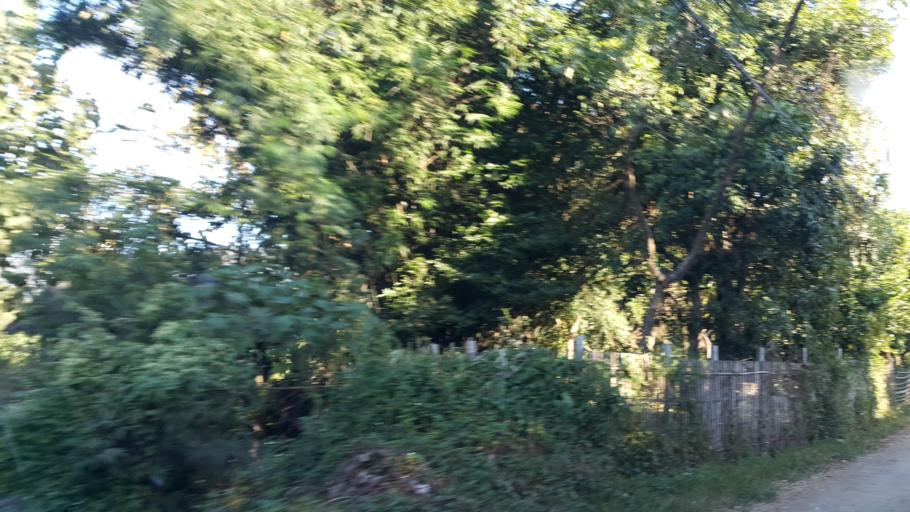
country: TH
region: Chiang Mai
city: Mae On
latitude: 18.7546
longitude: 99.2583
